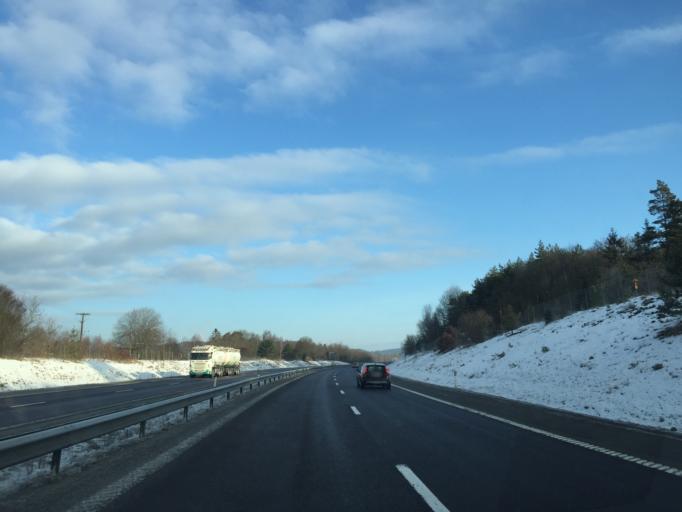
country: SE
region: Vaestra Goetaland
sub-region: Stenungsunds Kommun
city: Stora Hoga
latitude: 58.0392
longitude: 11.8462
